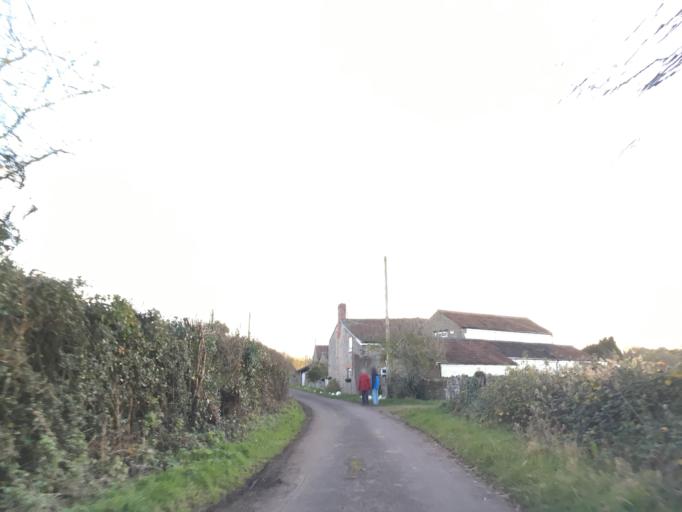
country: GB
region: England
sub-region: South Gloucestershire
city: Thornbury
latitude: 51.6122
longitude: -2.5001
